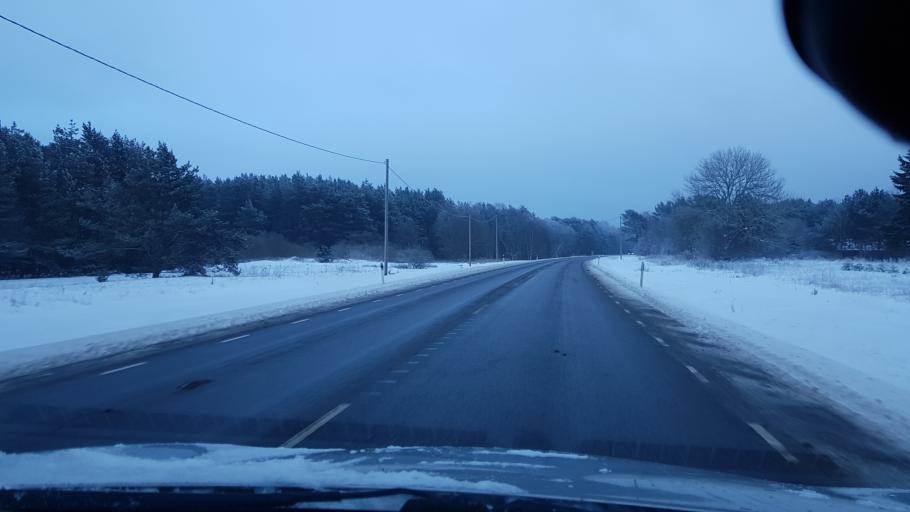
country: EE
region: Harju
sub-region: Paldiski linn
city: Paldiski
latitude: 59.3393
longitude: 24.2116
